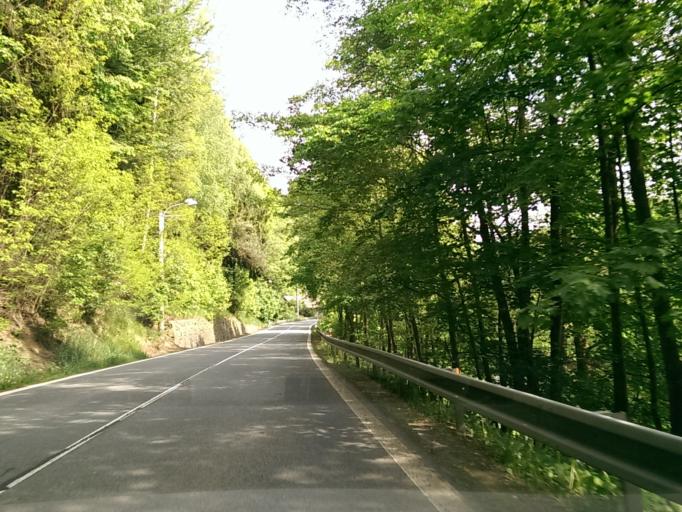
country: CZ
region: Liberecky
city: Zelezny Brod
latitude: 50.6447
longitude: 15.2348
